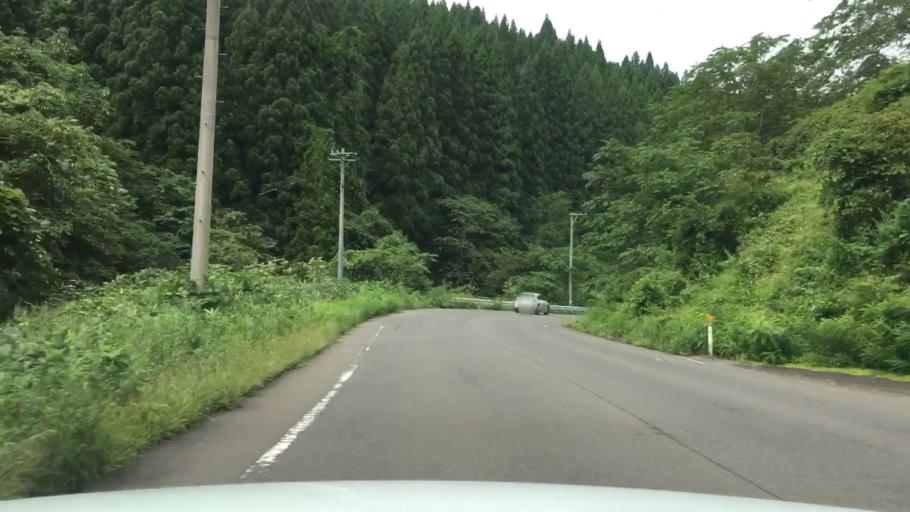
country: JP
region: Aomori
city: Shimokizukuri
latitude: 40.7293
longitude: 140.2528
